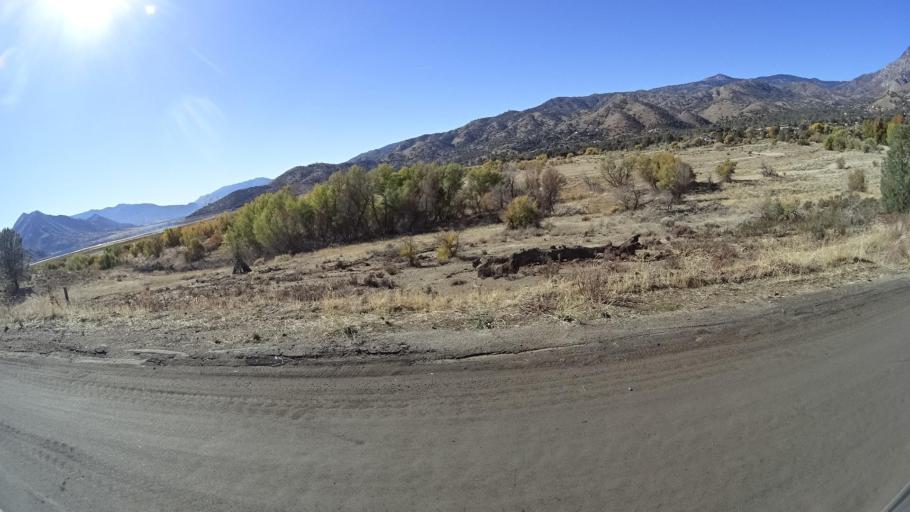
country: US
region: California
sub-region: Kern County
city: Wofford Heights
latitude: 35.7042
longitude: -118.4450
